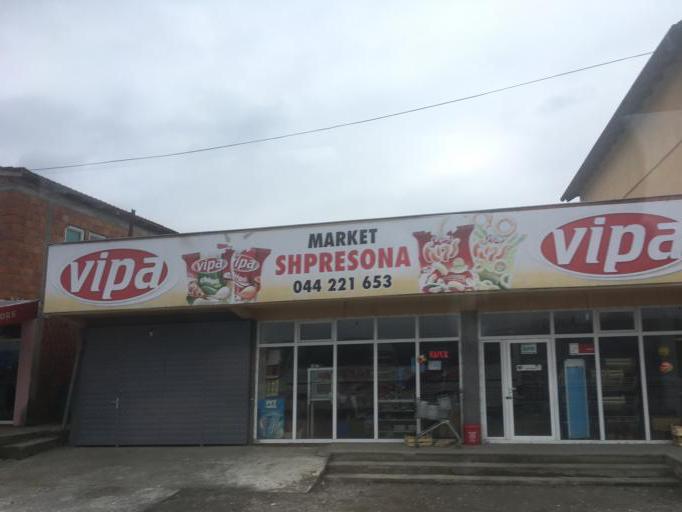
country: XK
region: Pristina
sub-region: Komuna e Drenasit
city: Glogovac
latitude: 42.5762
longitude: 20.8663
